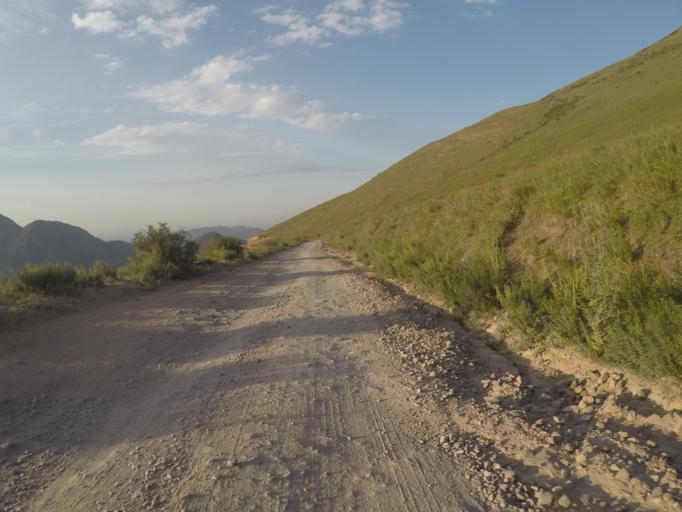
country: KG
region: Chuy
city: Bishkek
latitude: 42.6531
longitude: 74.6622
